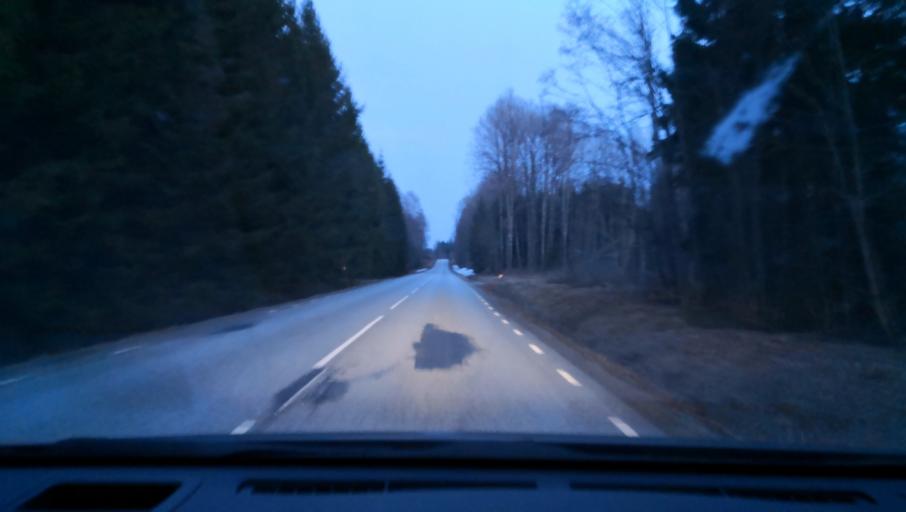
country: SE
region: OErebro
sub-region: Lindesbergs Kommun
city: Frovi
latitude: 59.5929
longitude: 15.4241
